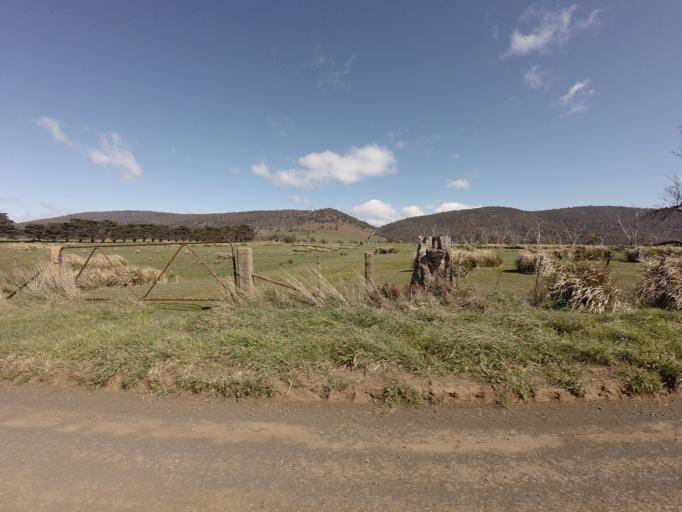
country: AU
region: Tasmania
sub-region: Northern Midlands
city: Evandale
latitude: -41.9486
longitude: 147.4337
